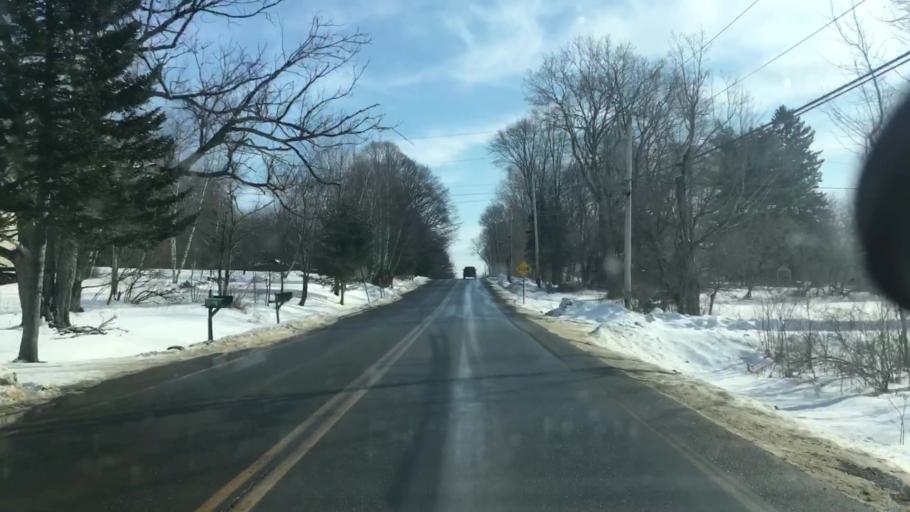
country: US
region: Maine
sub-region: Penobscot County
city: Bangor
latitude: 44.8496
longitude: -68.8412
